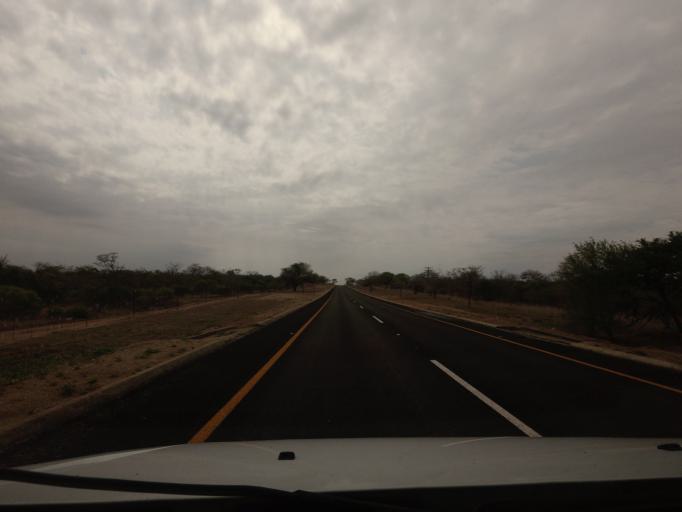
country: ZA
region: Limpopo
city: Thulamahashi
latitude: -24.5563
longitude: 31.2213
